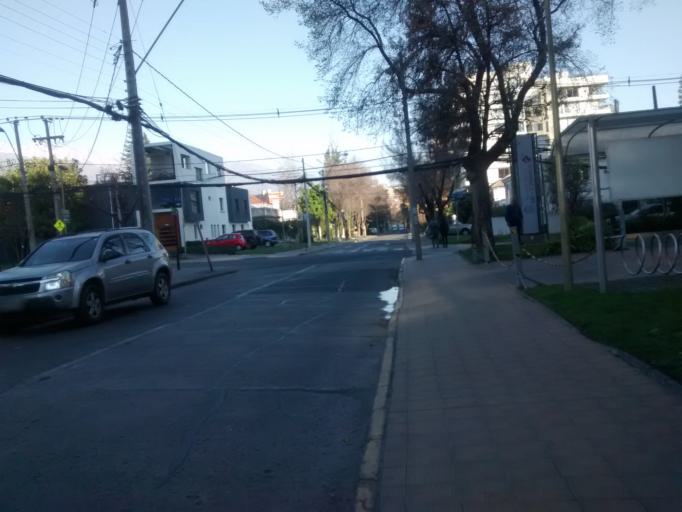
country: CL
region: Santiago Metropolitan
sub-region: Provincia de Santiago
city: Villa Presidente Frei, Nunoa, Santiago, Chile
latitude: -33.4152
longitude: -70.5827
